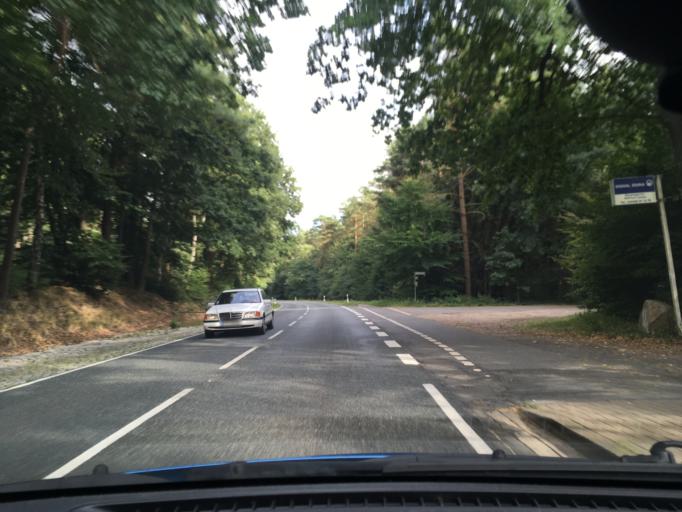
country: DE
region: Lower Saxony
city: Neu Wulmstorf
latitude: 53.4069
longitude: 9.8236
